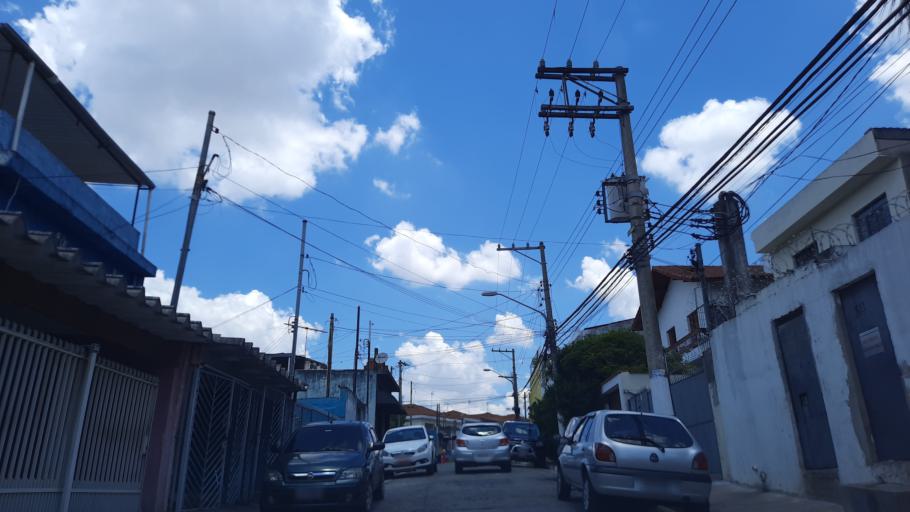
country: BR
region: Sao Paulo
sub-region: Sao Paulo
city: Sao Paulo
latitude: -23.4897
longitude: -46.6814
